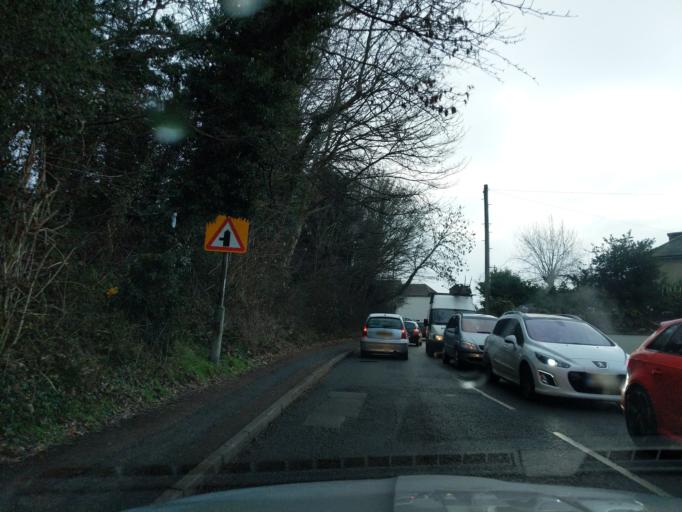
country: GB
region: England
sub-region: Hertfordshire
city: Abbots Langley
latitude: 51.7017
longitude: -0.4352
